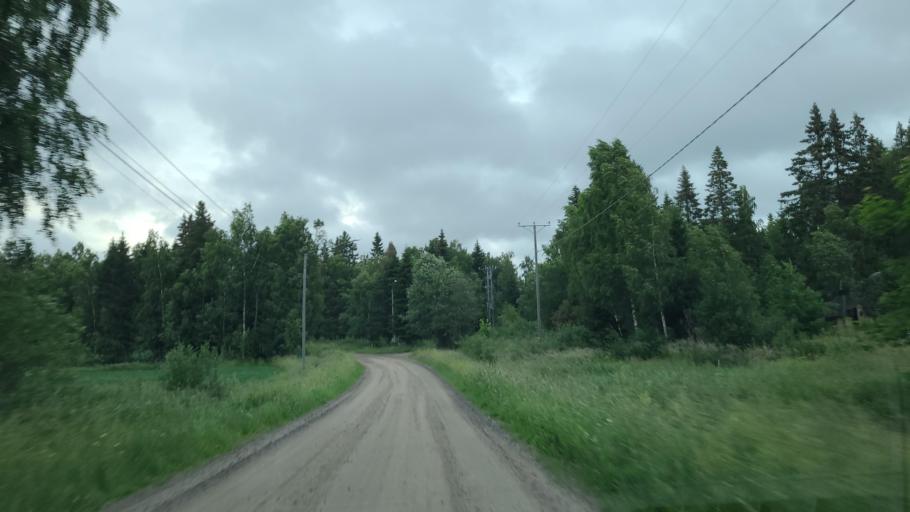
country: FI
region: Ostrobothnia
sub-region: Vaasa
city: Replot
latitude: 63.3128
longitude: 21.1600
